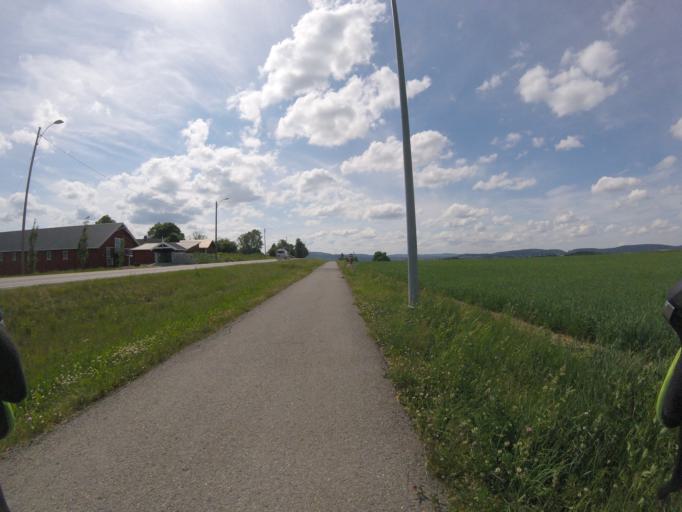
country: NO
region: Akershus
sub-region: Skedsmo
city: Lillestrom
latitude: 59.9903
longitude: 11.0482
